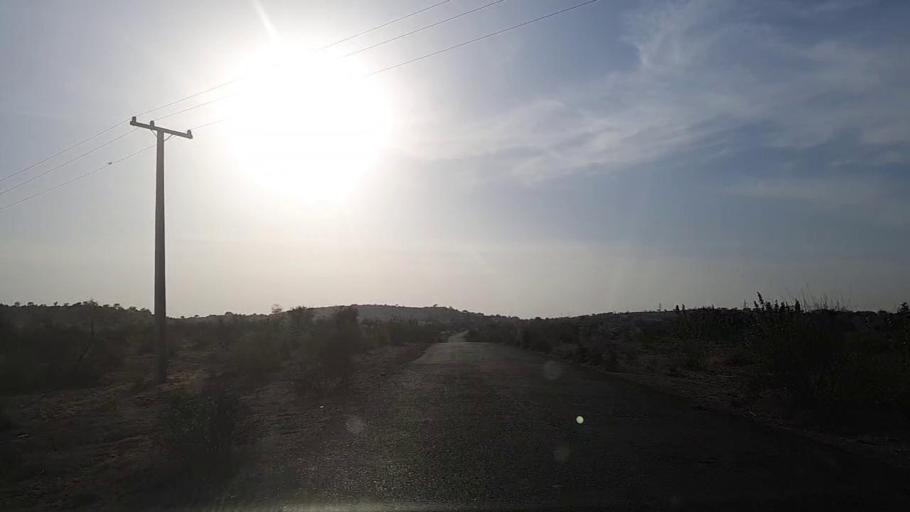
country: PK
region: Sindh
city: Umarkot
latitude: 25.1672
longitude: 70.0431
